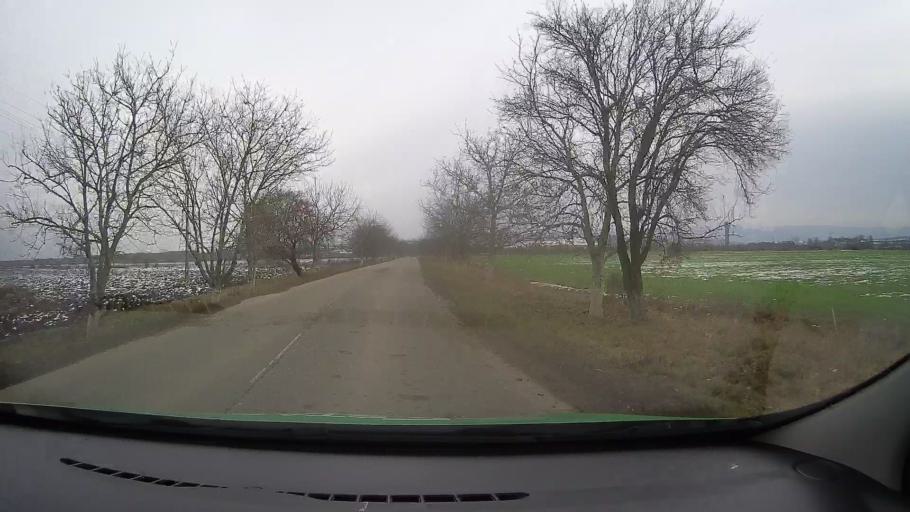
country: RO
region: Hunedoara
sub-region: Comuna Romos
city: Romos
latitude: 45.8828
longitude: 23.2522
